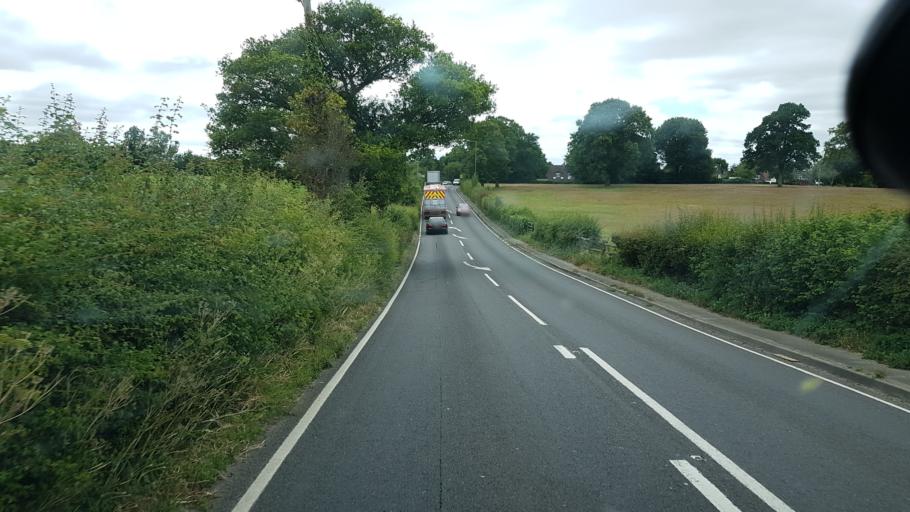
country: GB
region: England
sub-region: Surrey
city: Godstone
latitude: 51.2238
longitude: -0.0469
